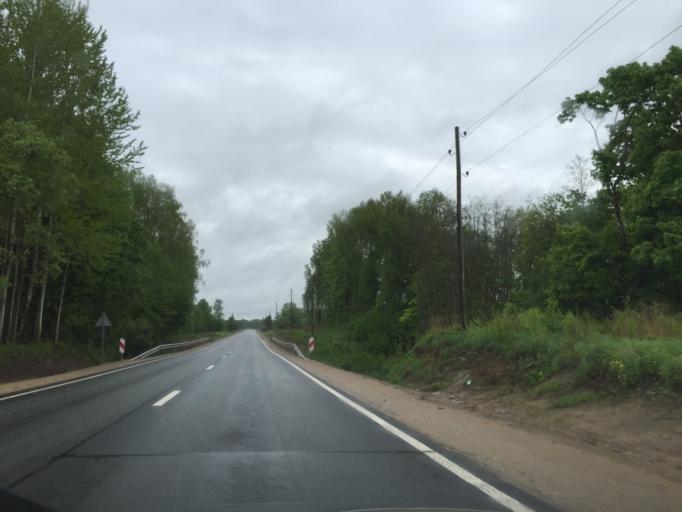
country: LV
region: Ogre
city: Jumprava
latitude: 56.6904
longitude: 24.8944
